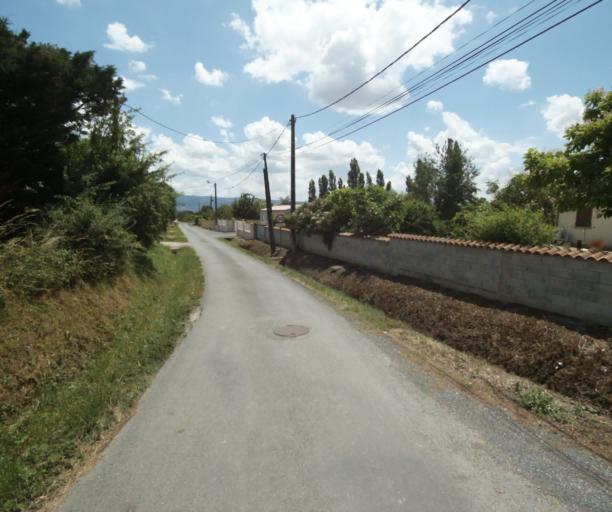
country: FR
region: Midi-Pyrenees
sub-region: Departement du Tarn
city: Soual
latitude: 43.5403
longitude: 2.0619
